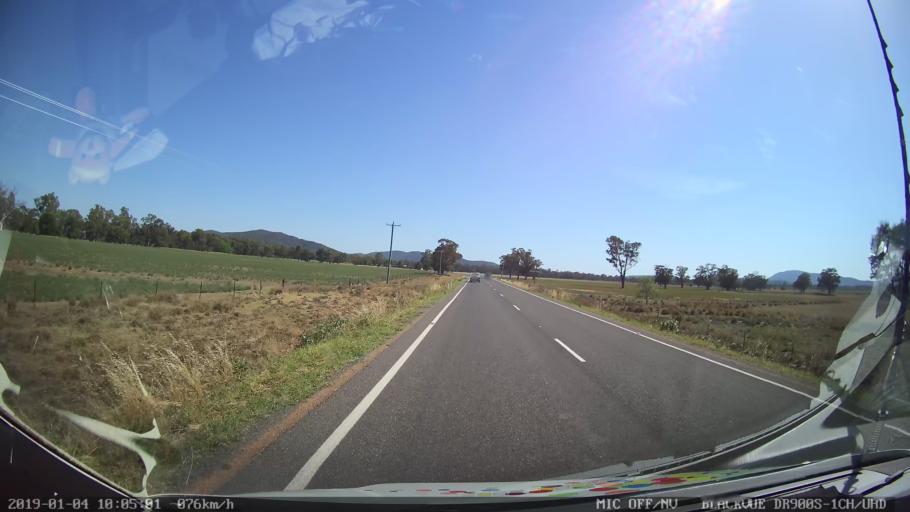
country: AU
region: New South Wales
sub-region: Cabonne
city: Canowindra
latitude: -33.4465
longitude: 148.3636
